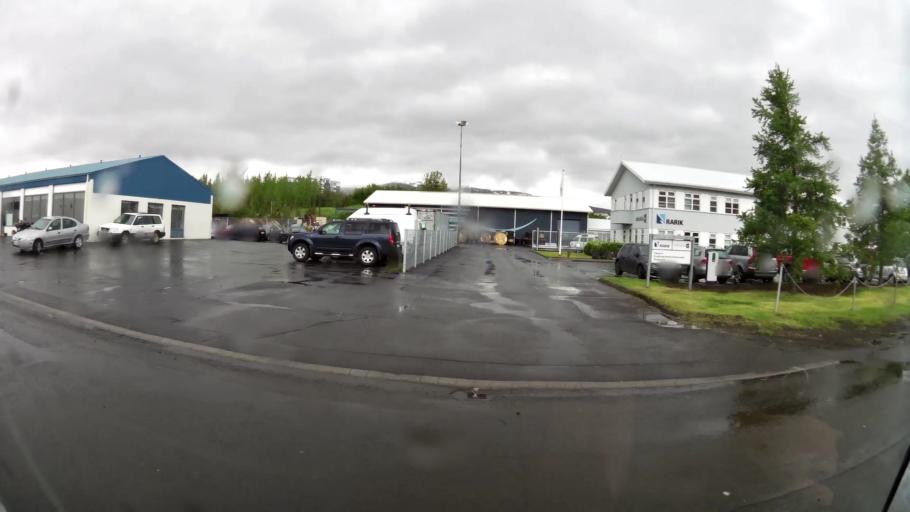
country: IS
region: Northeast
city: Akureyri
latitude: 65.6939
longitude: -18.1010
